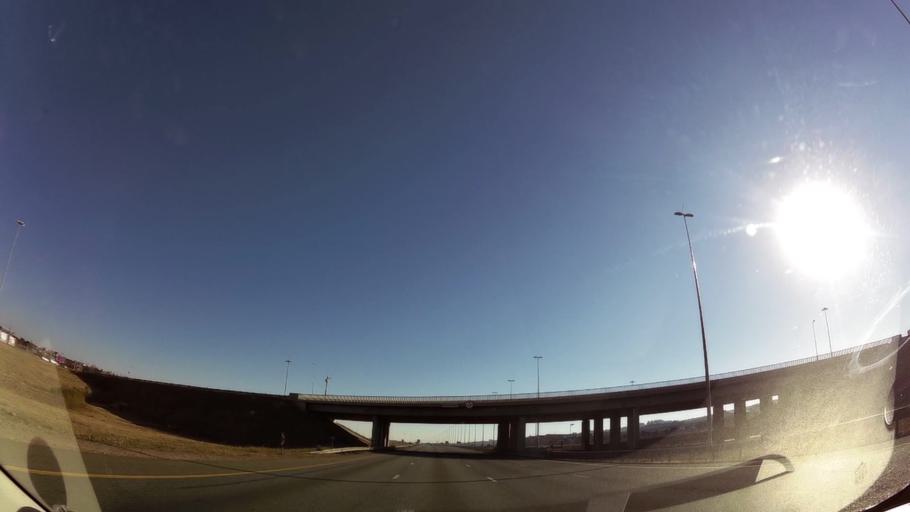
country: ZA
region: Gauteng
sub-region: City of Tshwane Metropolitan Municipality
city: Centurion
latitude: -25.8654
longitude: 28.2536
